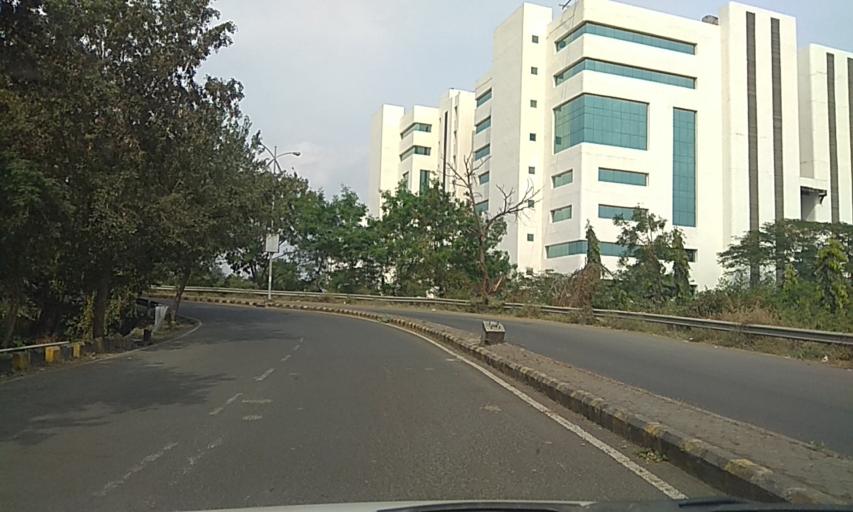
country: IN
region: Maharashtra
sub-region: Pune Division
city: Pimpri
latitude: 18.5985
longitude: 73.7172
